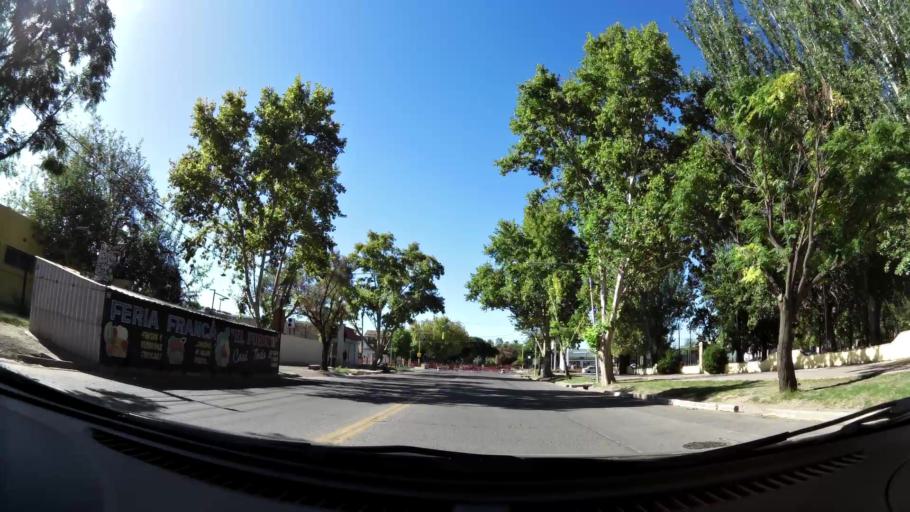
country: AR
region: Mendoza
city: Las Heras
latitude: -32.8430
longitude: -68.8195
